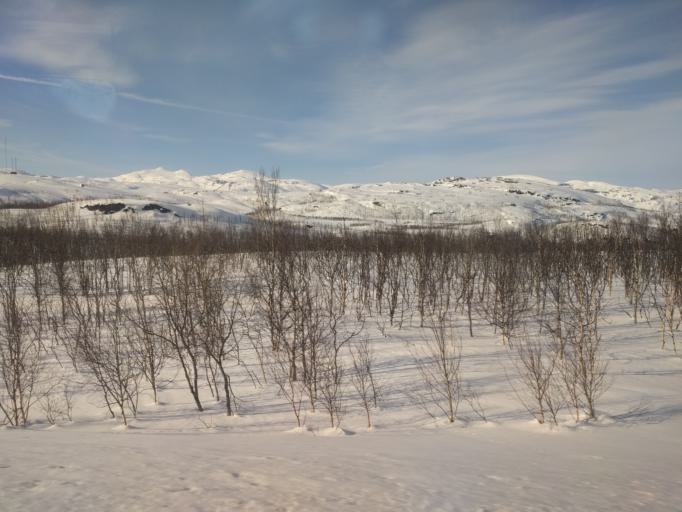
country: NO
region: Troms
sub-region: Bardu
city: Setermoen
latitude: 68.4216
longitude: 18.3020
